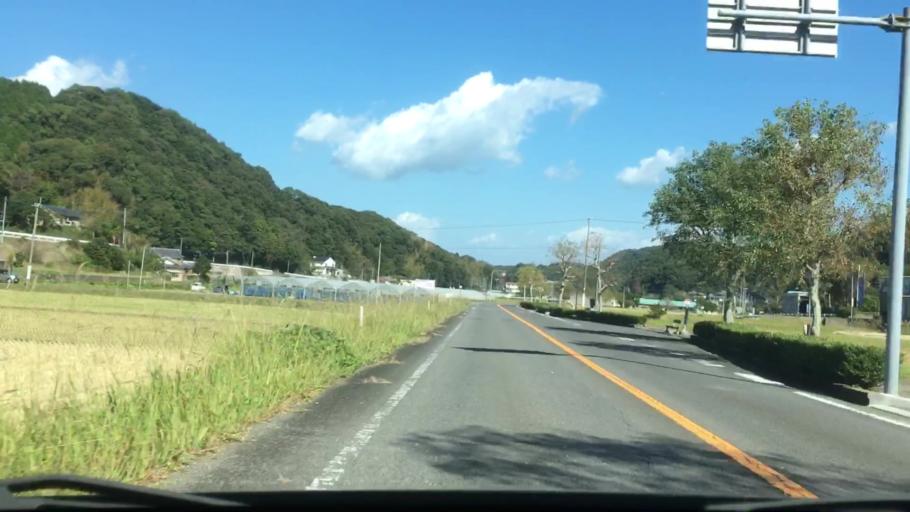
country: JP
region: Nagasaki
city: Sasebo
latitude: 32.9609
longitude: 129.6446
